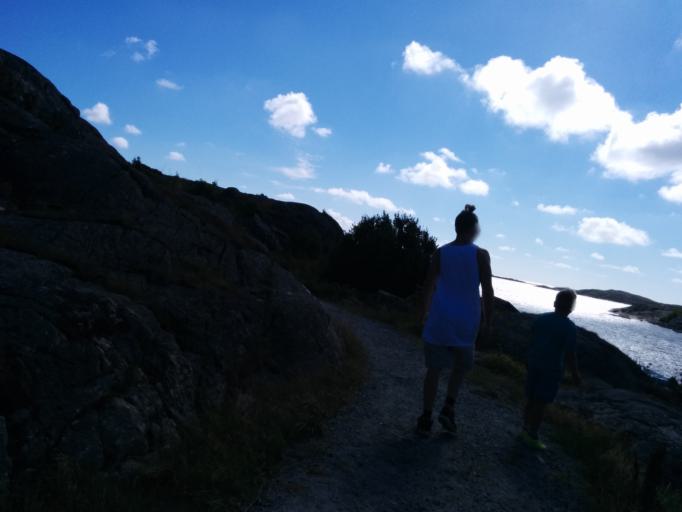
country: SE
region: Vaestra Goetaland
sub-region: Lysekils Kommun
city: Lysekil
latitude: 58.1234
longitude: 11.4392
